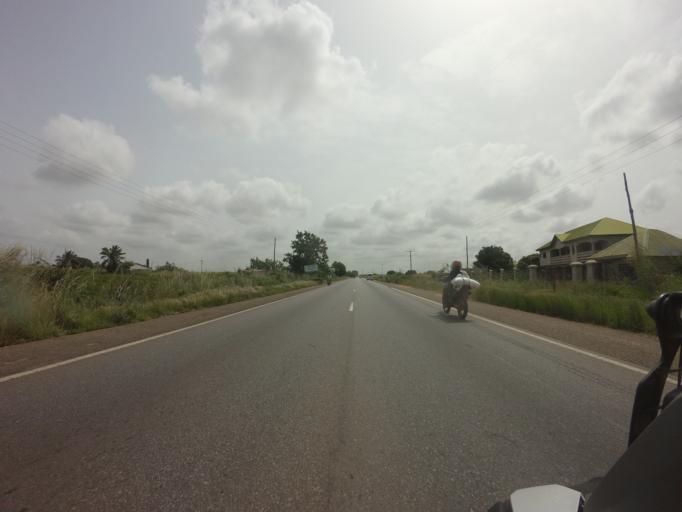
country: GH
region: Volta
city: Anloga
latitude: 5.8939
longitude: 0.5004
